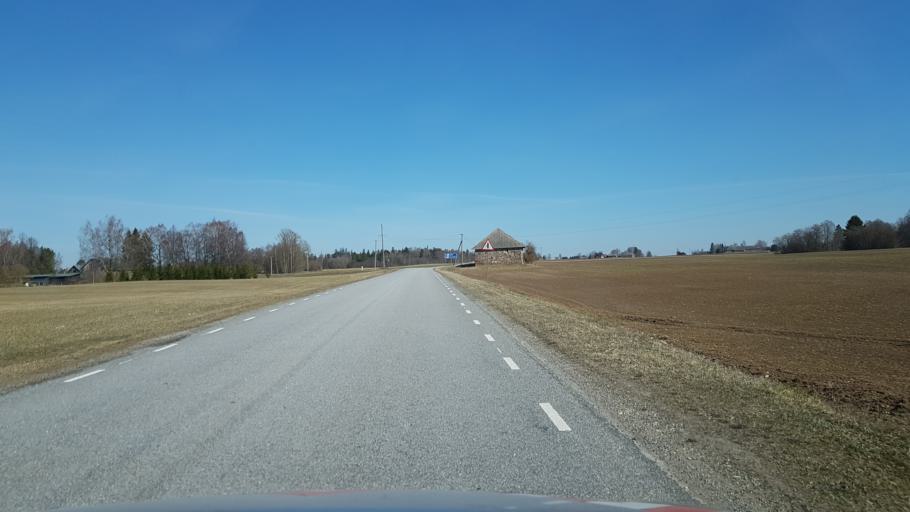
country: EE
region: Laeaene-Virumaa
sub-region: Vinni vald
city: Vinni
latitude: 59.2540
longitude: 26.3583
